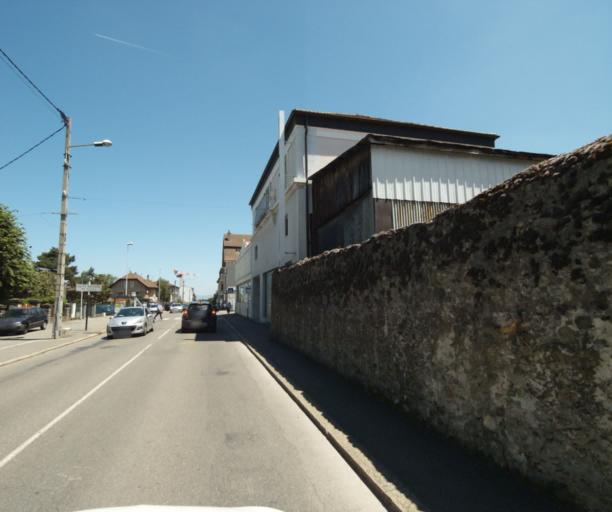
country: FR
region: Rhone-Alpes
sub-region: Departement de la Haute-Savoie
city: Thonon-les-Bains
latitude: 46.3752
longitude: 6.4840
